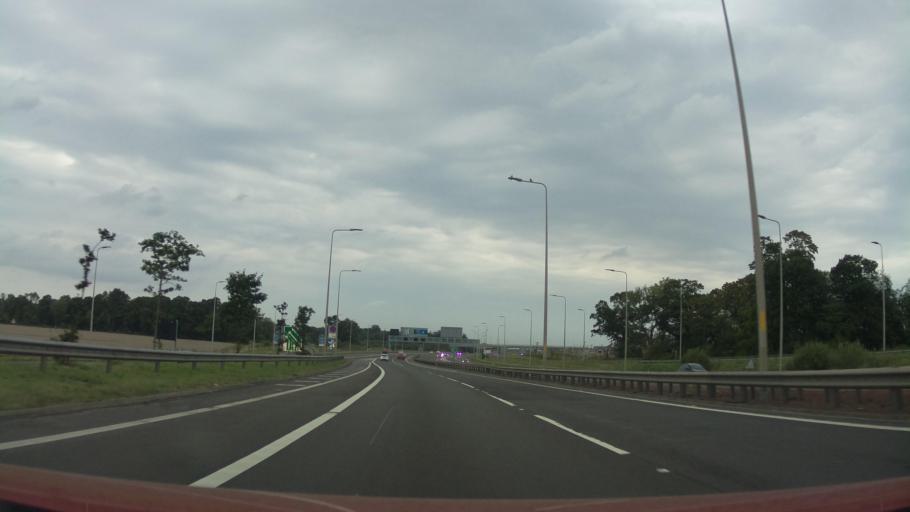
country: GB
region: Scotland
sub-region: Edinburgh
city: Queensferry
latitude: 55.9791
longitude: -3.3855
